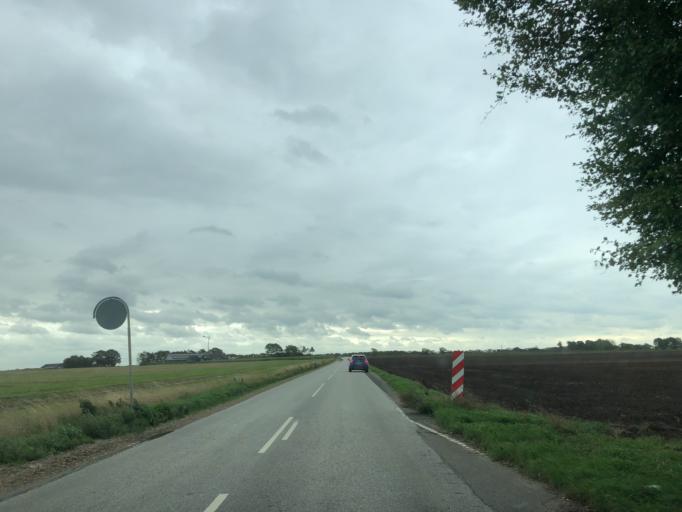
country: DK
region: Central Jutland
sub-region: Herning Kommune
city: Snejbjerg
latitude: 56.1509
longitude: 8.8937
